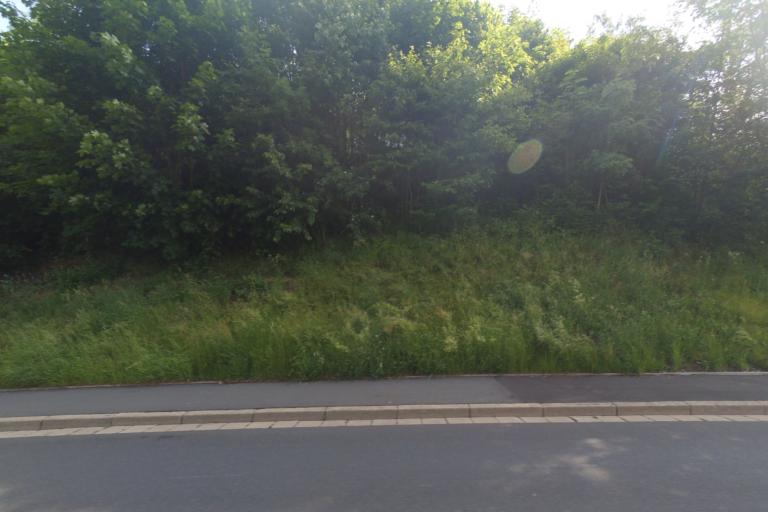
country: DE
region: Bavaria
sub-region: Upper Franconia
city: Ludwigsstadt
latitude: 50.4908
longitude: 11.3821
